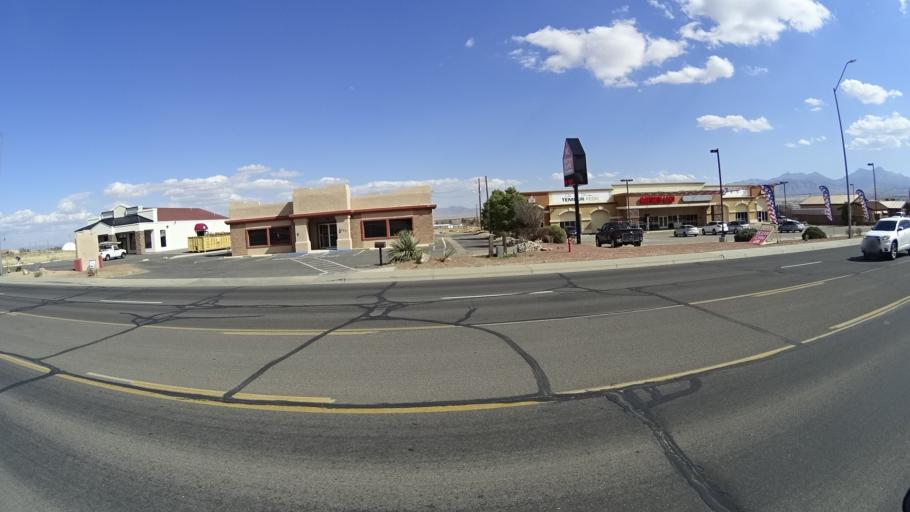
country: US
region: Arizona
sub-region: Mohave County
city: New Kingman-Butler
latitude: 35.2484
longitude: -114.0389
